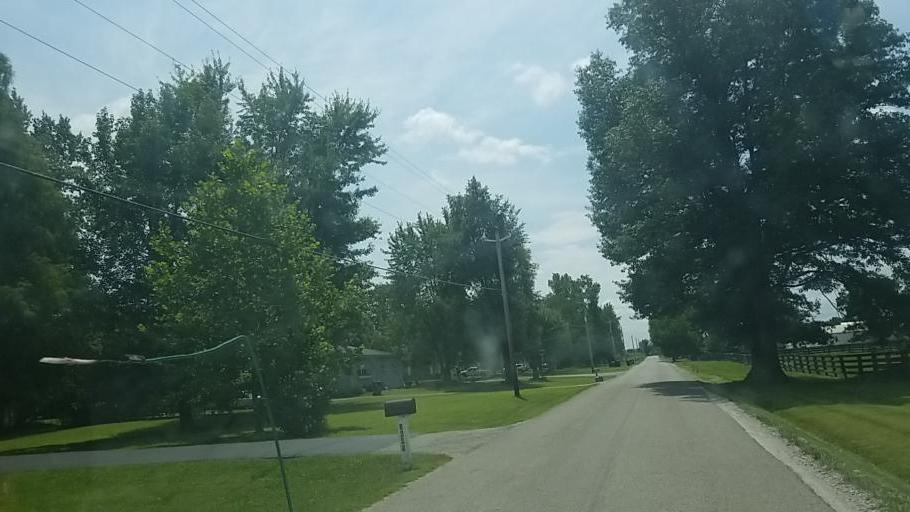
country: US
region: Ohio
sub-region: Franklin County
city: New Albany
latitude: 40.0326
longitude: -82.7690
